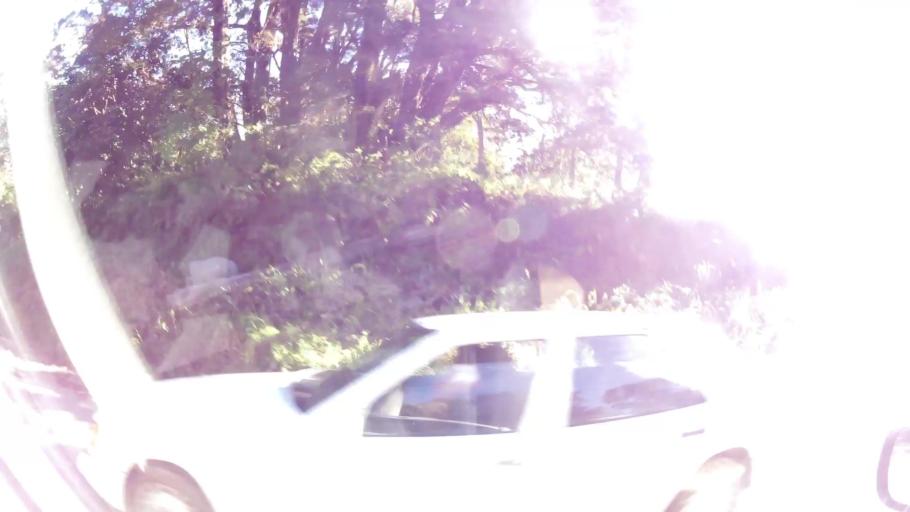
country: CR
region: Guanacaste
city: Juntas
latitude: 10.3057
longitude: -84.8117
